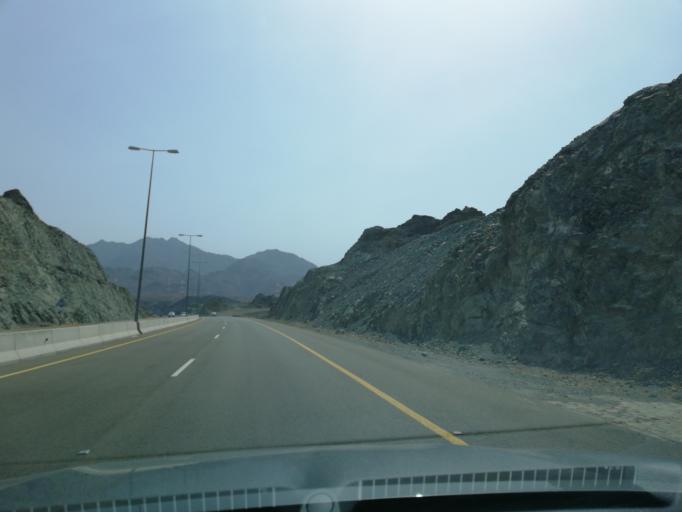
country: OM
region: Al Batinah
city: Al Liwa'
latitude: 24.2605
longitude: 56.3639
